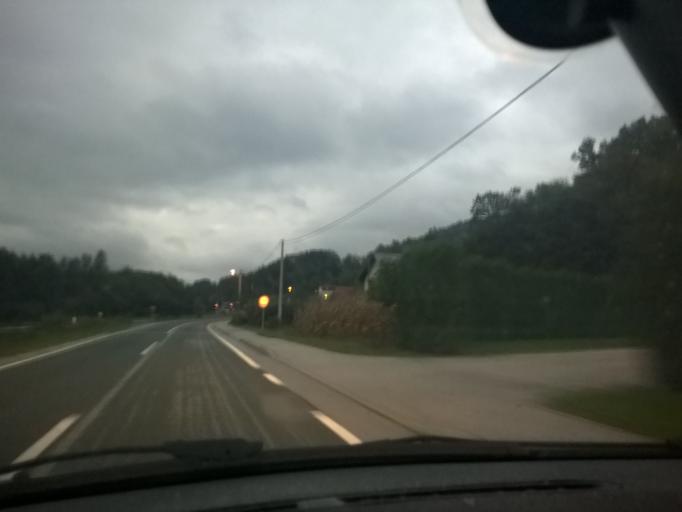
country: HR
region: Krapinsko-Zagorska
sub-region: Grad Krapina
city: Krapina
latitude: 46.2035
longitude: 15.8239
